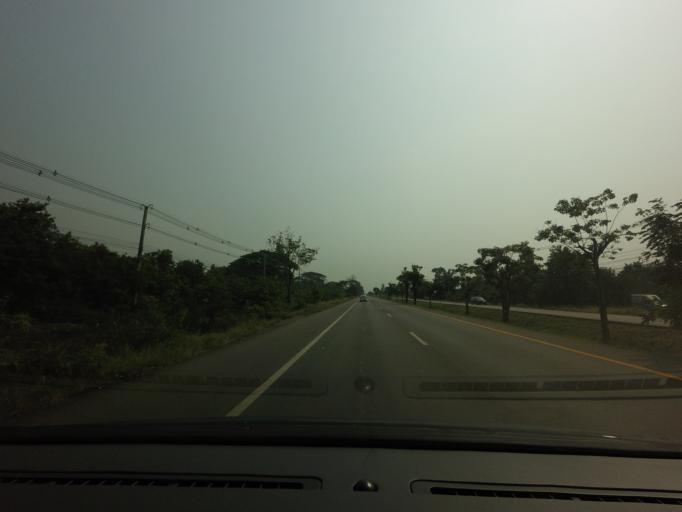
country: TH
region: Prachuap Khiri Khan
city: Kui Buri
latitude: 12.1087
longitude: 99.8534
